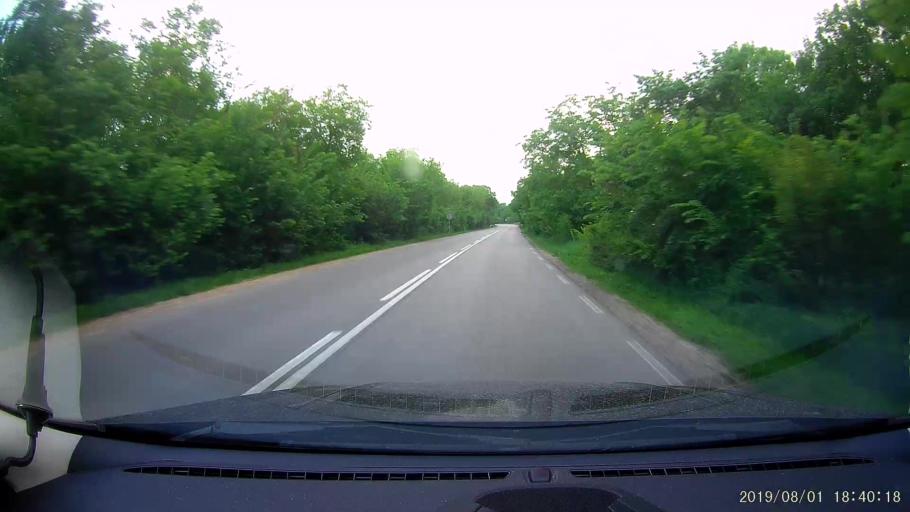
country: BG
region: Shumen
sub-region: Obshtina Khitrino
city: Gara Khitrino
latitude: 43.3697
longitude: 26.9199
